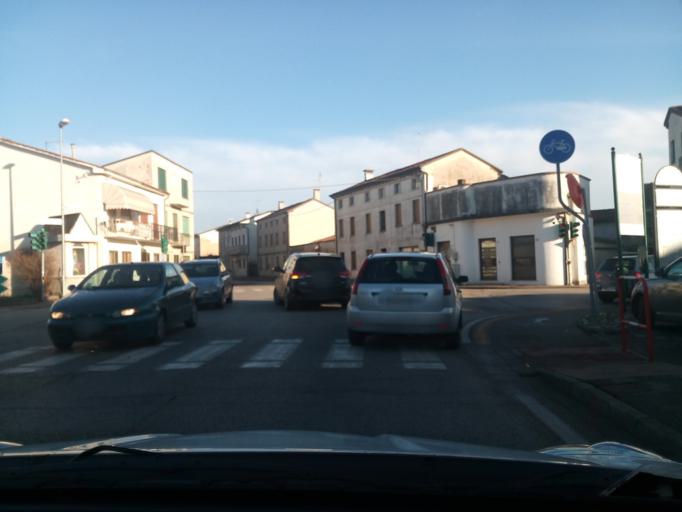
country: IT
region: Veneto
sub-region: Provincia di Vicenza
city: Dueville
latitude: 45.6397
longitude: 11.5511
